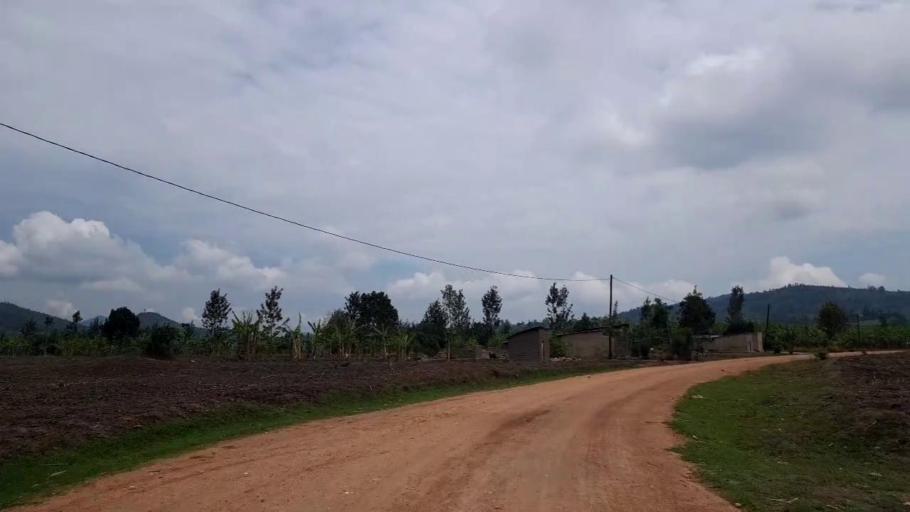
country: RW
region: Northern Province
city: Byumba
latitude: -1.4992
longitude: 30.2075
